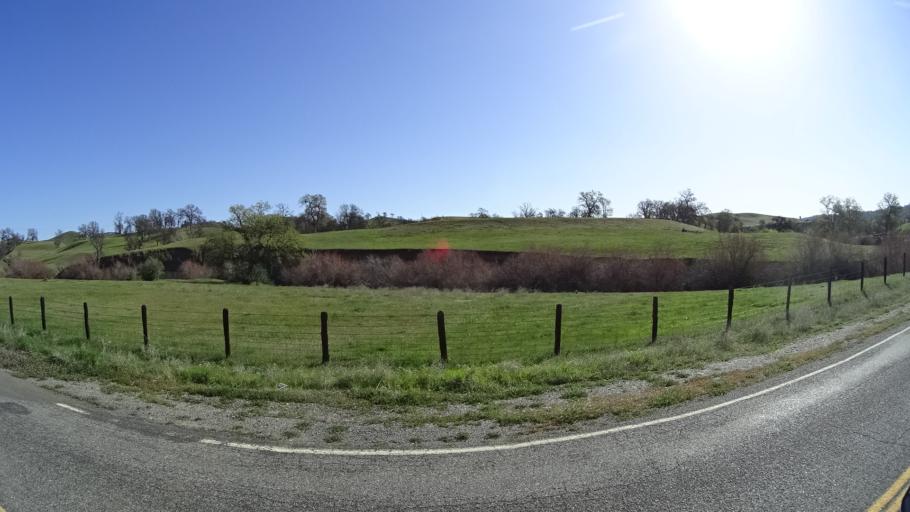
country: US
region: California
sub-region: Glenn County
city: Orland
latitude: 39.6819
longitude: -122.5353
